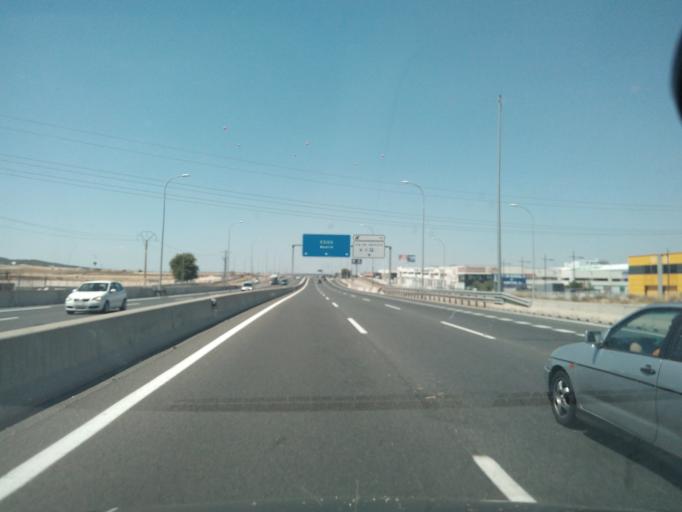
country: ES
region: Madrid
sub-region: Provincia de Madrid
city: Ciempozuelos
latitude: 40.1279
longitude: -3.6565
